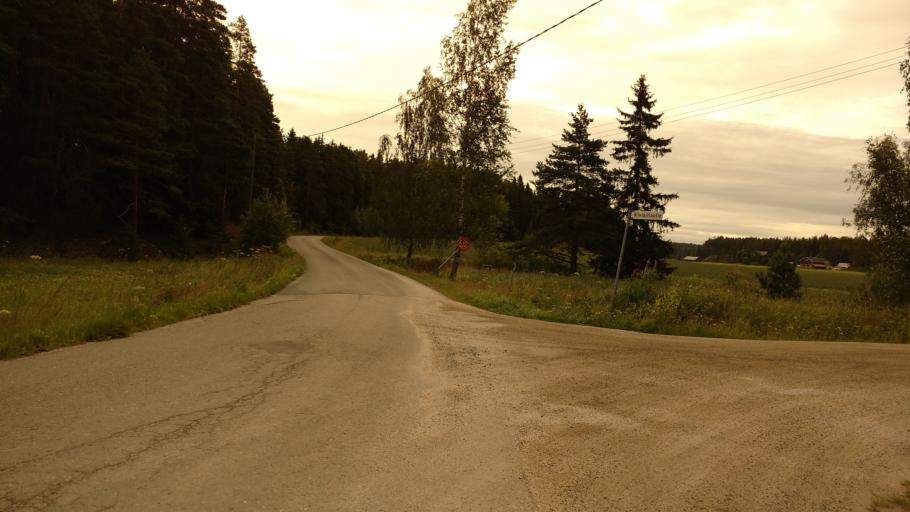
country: FI
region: Varsinais-Suomi
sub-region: Turku
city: Piikkioe
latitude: 60.4321
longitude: 22.4573
